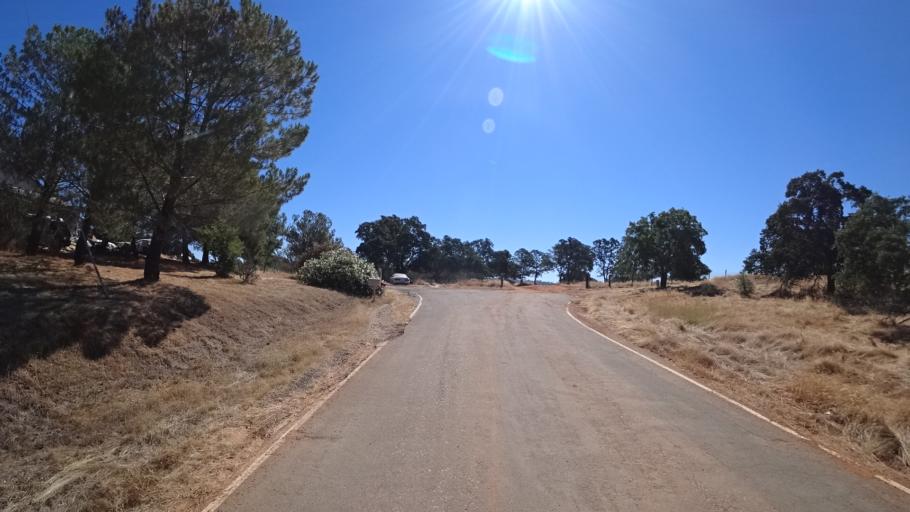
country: US
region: California
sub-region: Calaveras County
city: Rancho Calaveras
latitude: 38.1084
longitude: -120.8591
